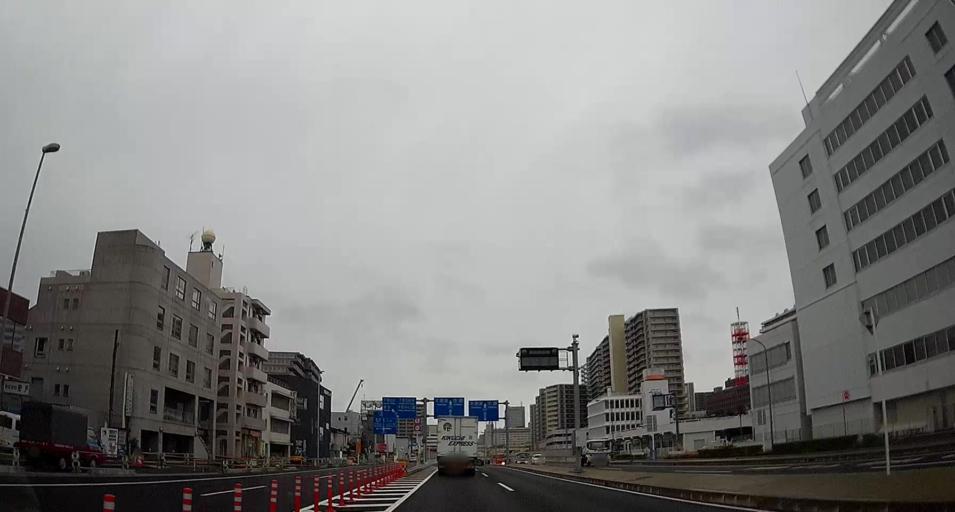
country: JP
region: Chiba
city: Chiba
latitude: 35.6140
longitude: 140.1030
